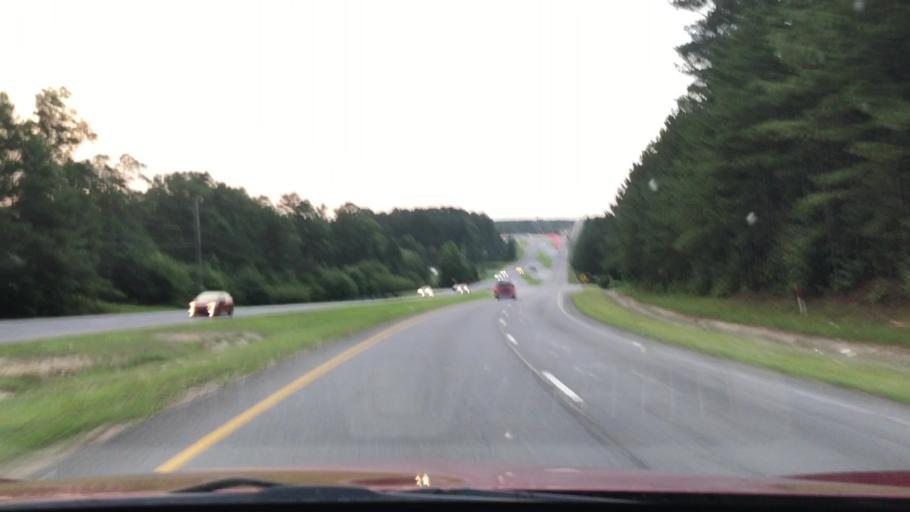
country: US
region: Georgia
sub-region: Gwinnett County
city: Lawrenceville
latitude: 33.9982
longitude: -83.9902
